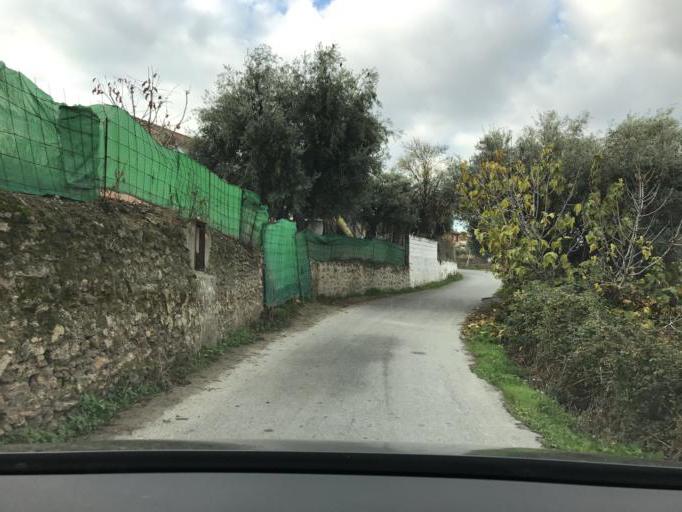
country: ES
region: Andalusia
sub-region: Provincia de Granada
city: Zubia
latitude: 37.1253
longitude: -3.5803
